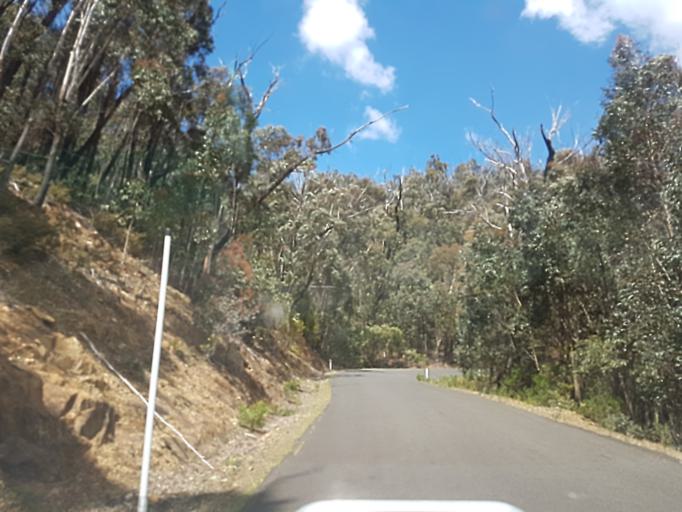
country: AU
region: Victoria
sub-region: East Gippsland
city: Bairnsdale
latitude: -37.3872
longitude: 147.2219
